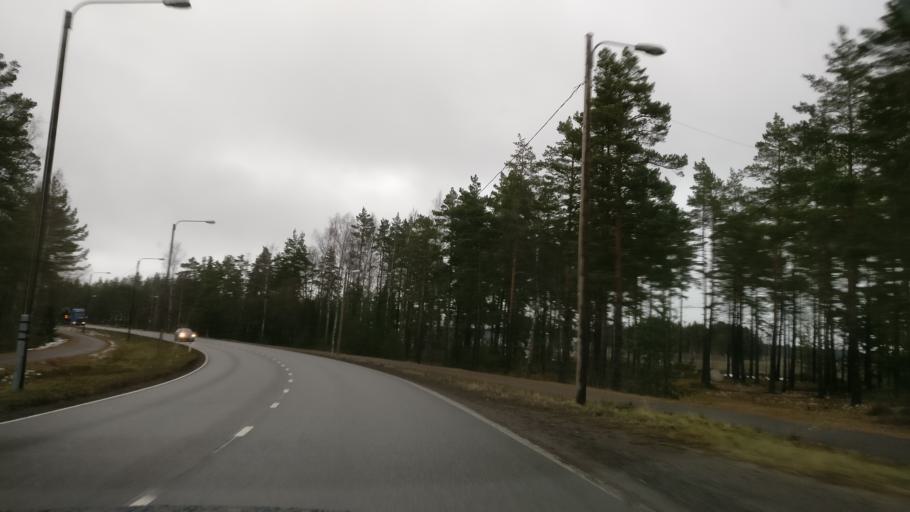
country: FI
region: Uusimaa
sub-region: Raaseporin
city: Hanko
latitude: 59.8436
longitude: 23.0075
